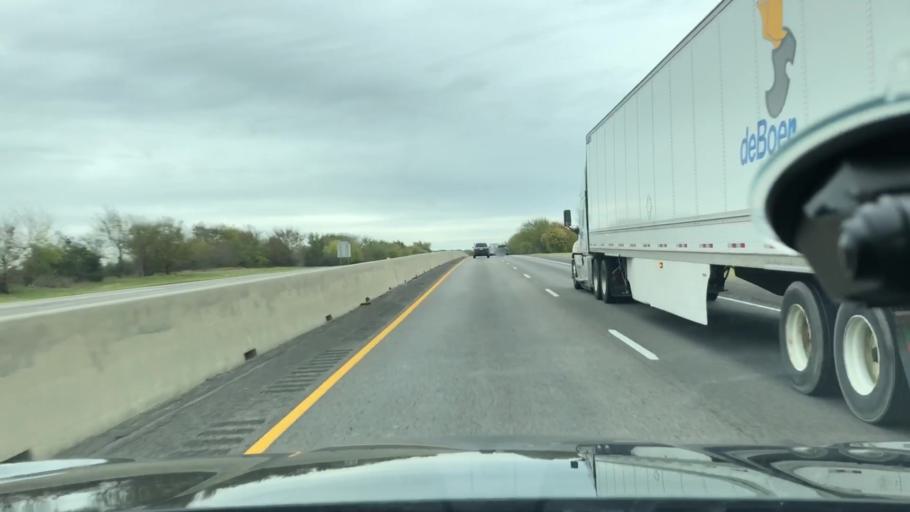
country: US
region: Texas
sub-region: Franklin County
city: Mount Vernon
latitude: 33.1630
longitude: -95.4022
